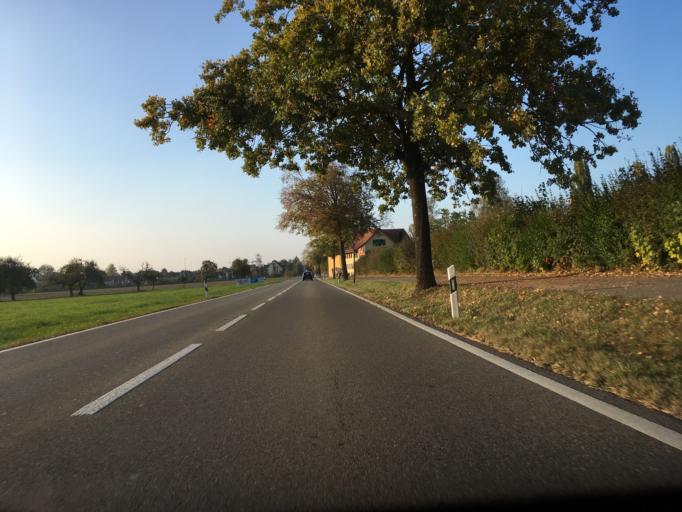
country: CH
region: Zurich
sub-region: Bezirk Pfaeffikon
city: Fehraltorf
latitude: 47.3805
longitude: 8.7629
